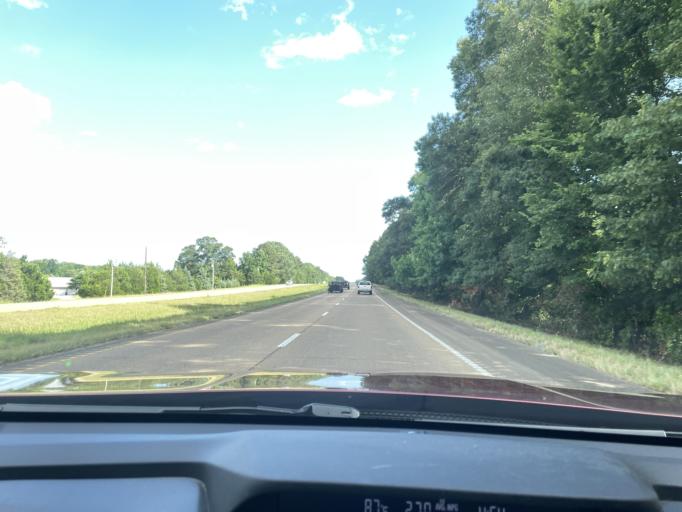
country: US
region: Mississippi
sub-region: Madison County
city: Flora
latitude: 32.5024
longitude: -90.2996
